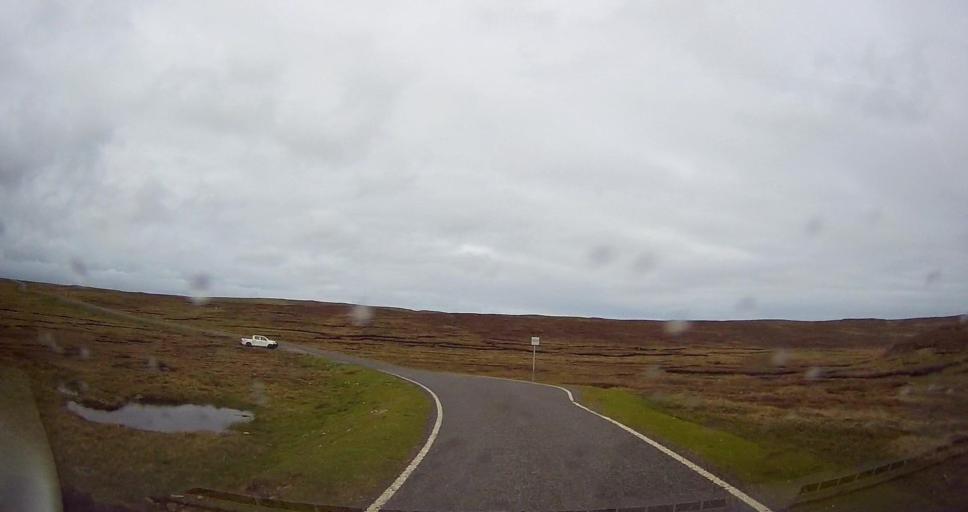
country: GB
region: Scotland
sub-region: Shetland Islands
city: Lerwick
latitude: 60.4914
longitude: -1.5779
